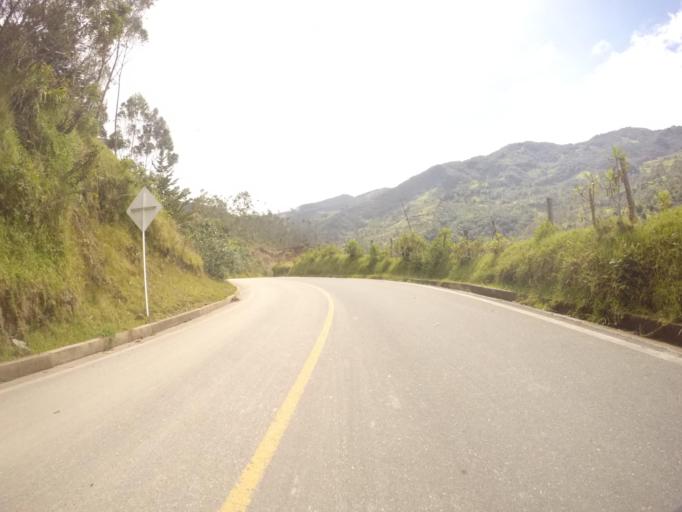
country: CO
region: Cauca
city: Jambalo
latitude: 2.7262
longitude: -76.3244
